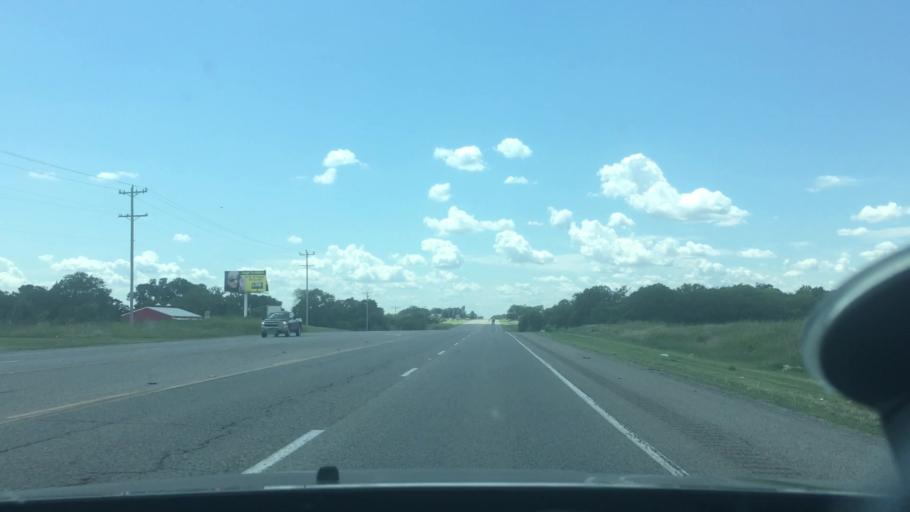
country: US
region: Oklahoma
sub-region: Bryan County
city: Calera
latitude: 33.9983
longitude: -96.4794
